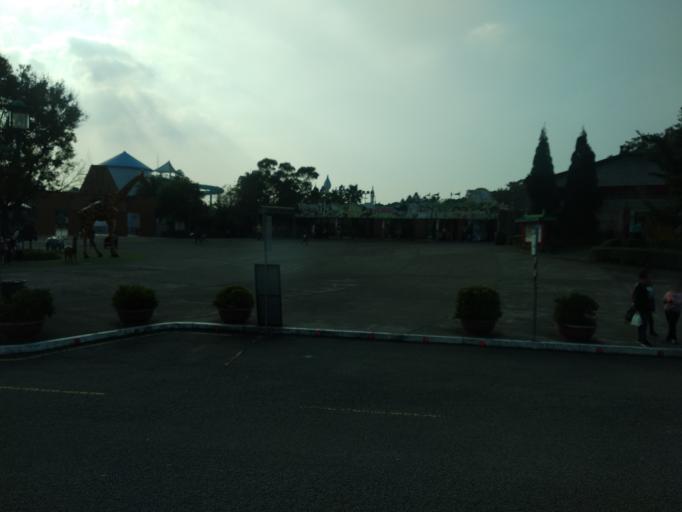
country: TW
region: Taiwan
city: Daxi
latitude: 24.8218
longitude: 121.1849
